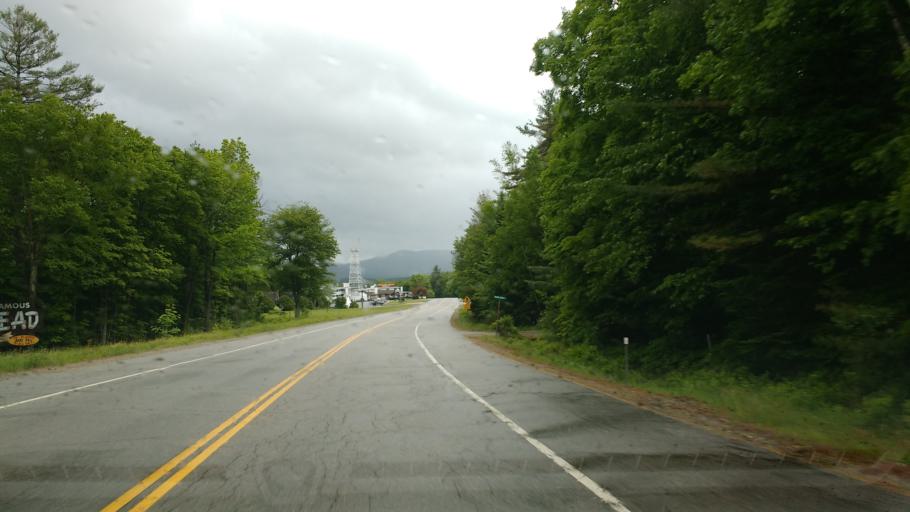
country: US
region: New Hampshire
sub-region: Grafton County
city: Woodstock
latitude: 44.0878
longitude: -71.6836
